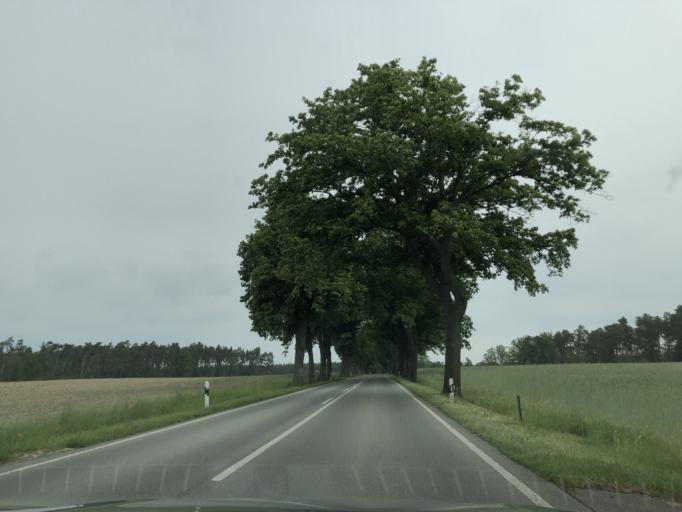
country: DE
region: Brandenburg
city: Plattenburg
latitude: 52.9290
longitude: 12.0845
